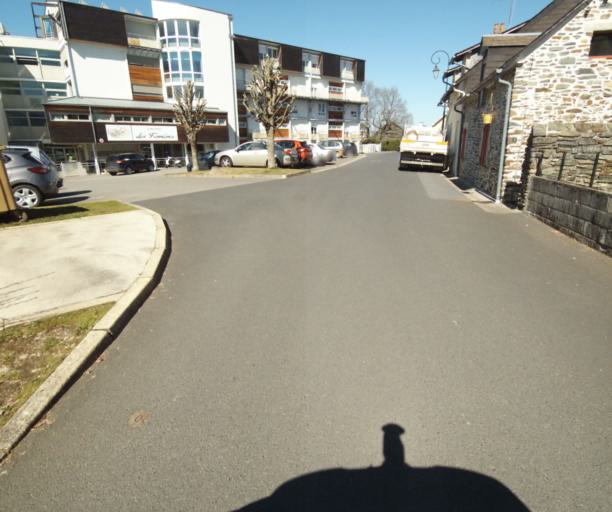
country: FR
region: Limousin
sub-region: Departement de la Correze
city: Seilhac
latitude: 45.3665
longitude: 1.7177
